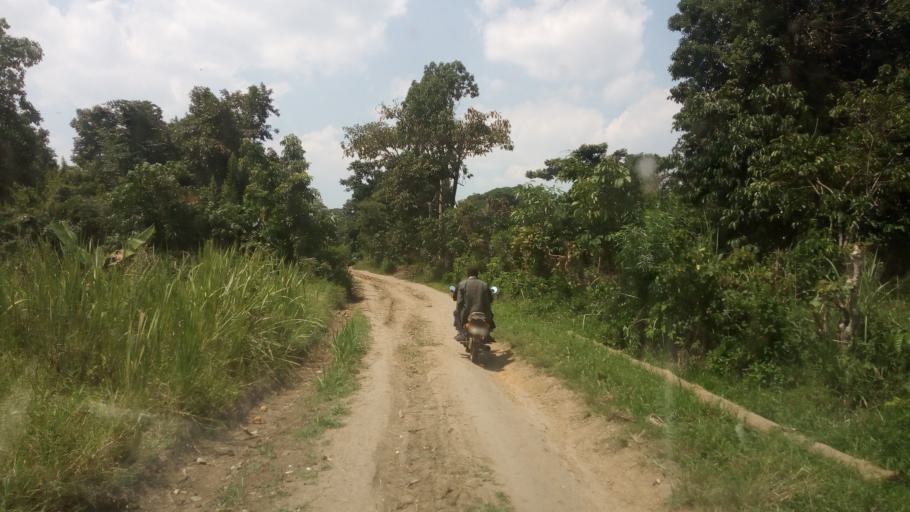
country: UG
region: Western Region
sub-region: Kanungu District
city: Ntungamo
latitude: -0.7785
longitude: 29.6497
